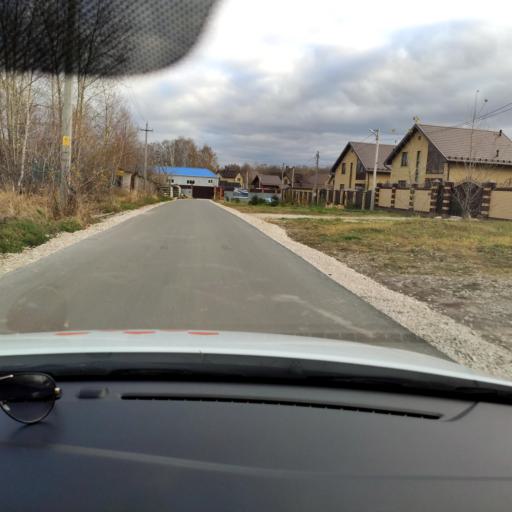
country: RU
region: Tatarstan
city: Stolbishchi
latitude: 55.7370
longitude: 49.2669
